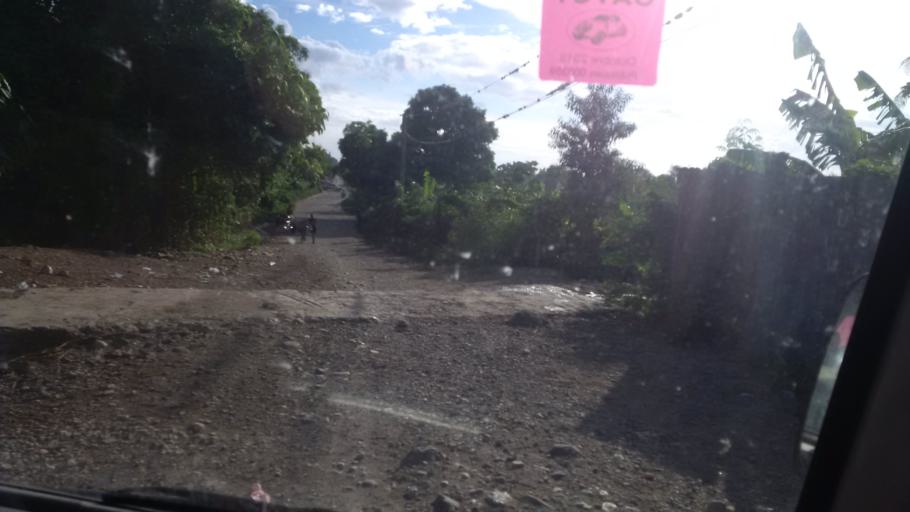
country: HT
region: Ouest
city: Thomazeau
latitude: 18.6553
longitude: -72.0825
